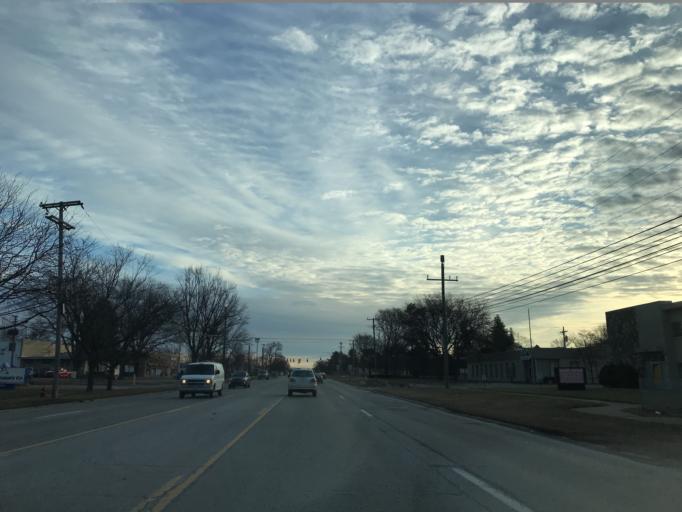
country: US
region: Michigan
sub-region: Oakland County
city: Farmington
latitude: 42.4412
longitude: -83.3491
